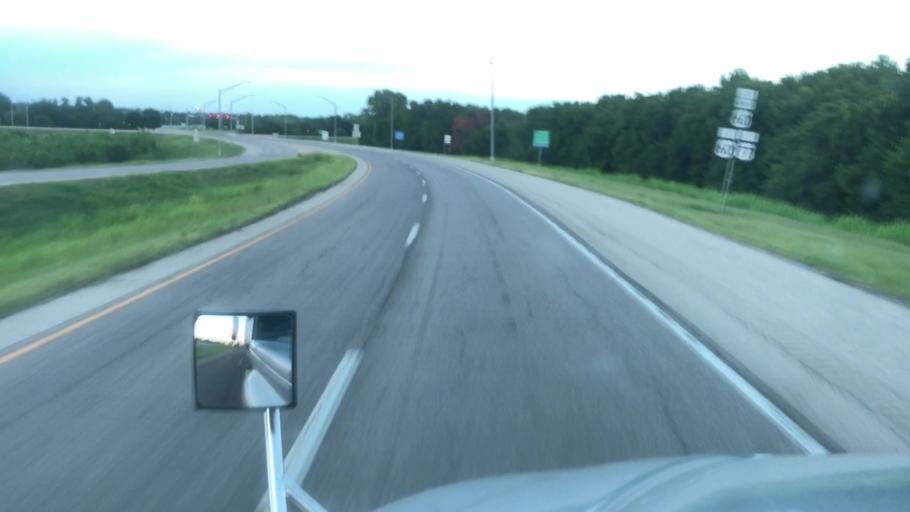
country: US
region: Oklahoma
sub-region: Kay County
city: Ponca City
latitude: 36.6776
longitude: -97.0708
